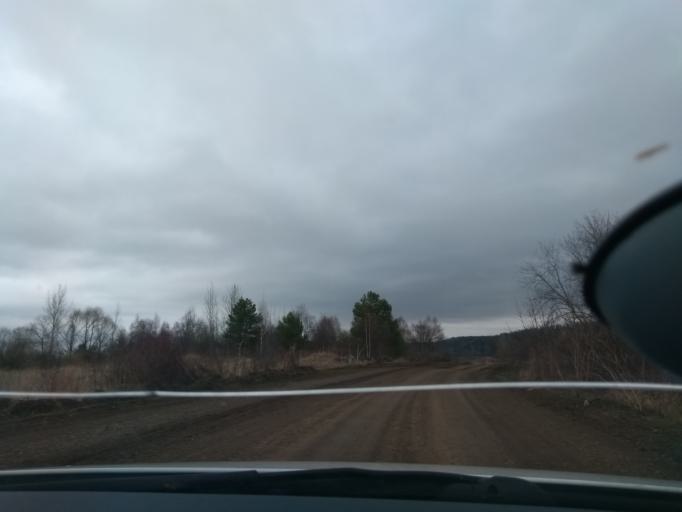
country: RU
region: Perm
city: Orda
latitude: 57.2479
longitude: 56.6132
